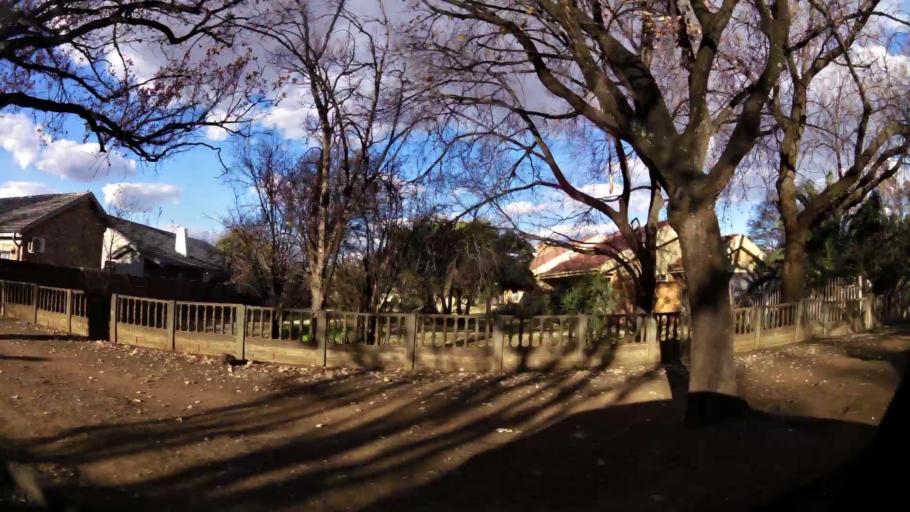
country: ZA
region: North-West
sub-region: Dr Kenneth Kaunda District Municipality
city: Potchefstroom
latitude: -26.7129
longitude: 27.0911
